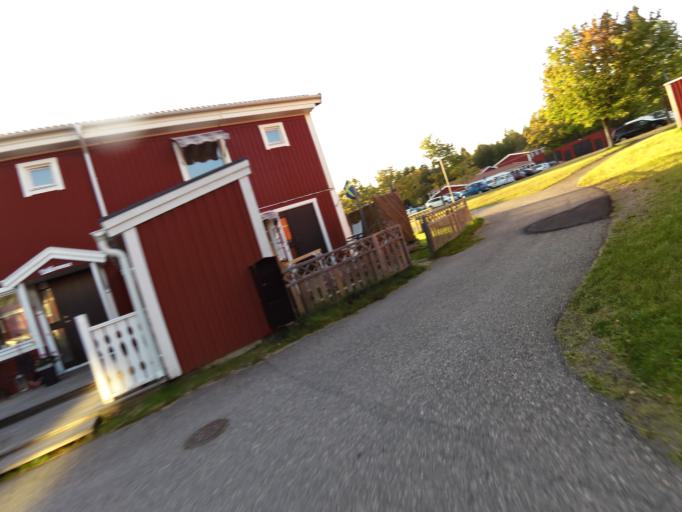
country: SE
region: Gaevleborg
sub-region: Gavle Kommun
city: Gavle
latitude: 60.6645
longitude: 17.2387
